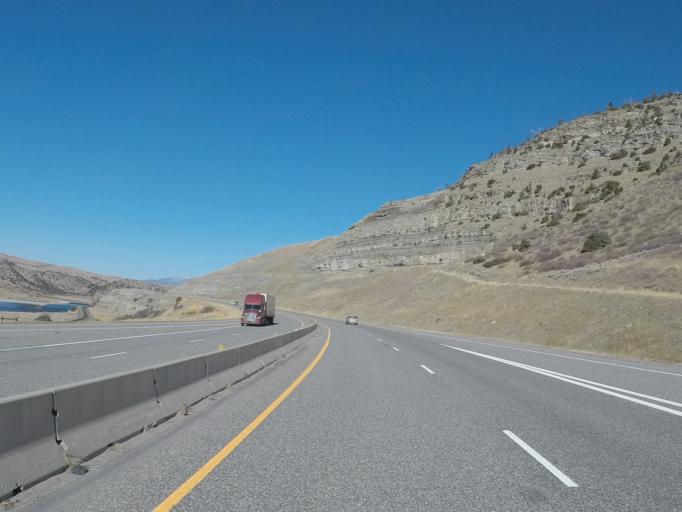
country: US
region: Montana
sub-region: Park County
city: Livingston
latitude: 45.7032
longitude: -110.2601
